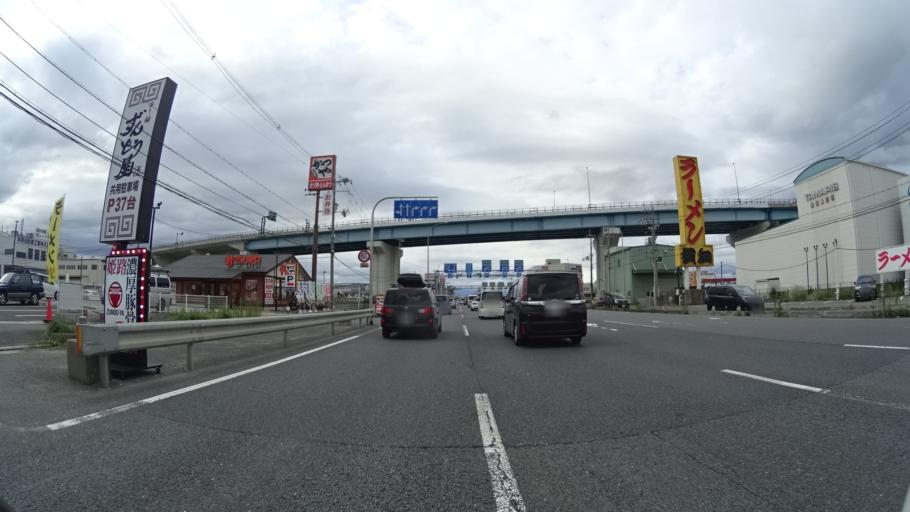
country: JP
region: Kyoto
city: Yawata
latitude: 34.8964
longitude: 135.7439
